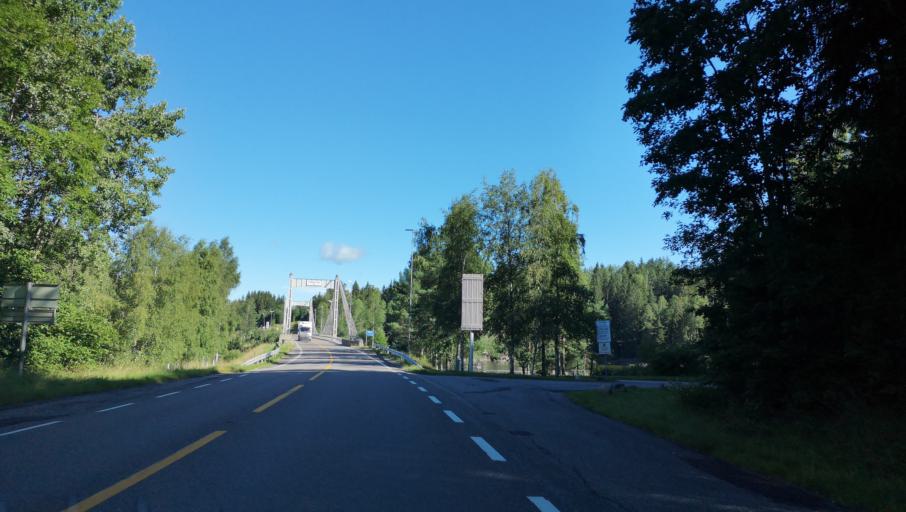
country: NO
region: Ostfold
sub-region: Spydeberg
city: Spydeberg
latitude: 59.6014
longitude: 11.1030
